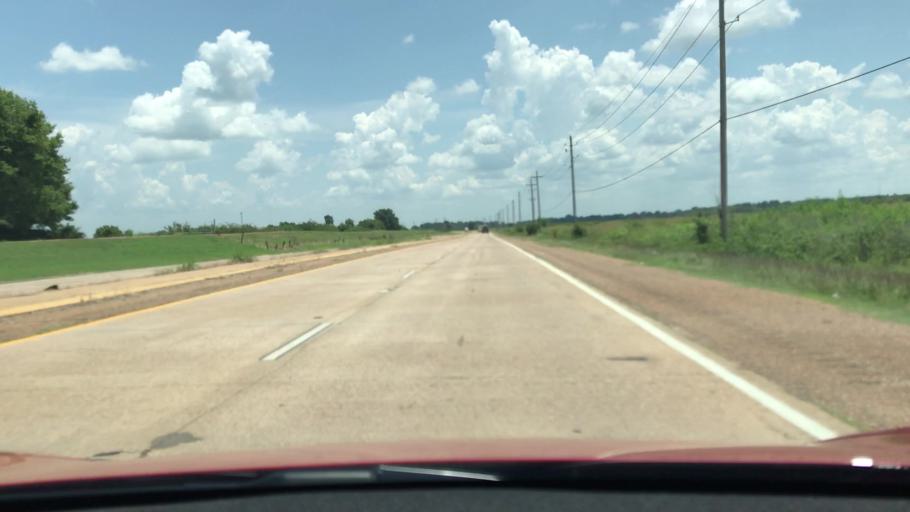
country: US
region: Louisiana
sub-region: Bossier Parish
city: Bossier City
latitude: 32.3952
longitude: -93.6883
